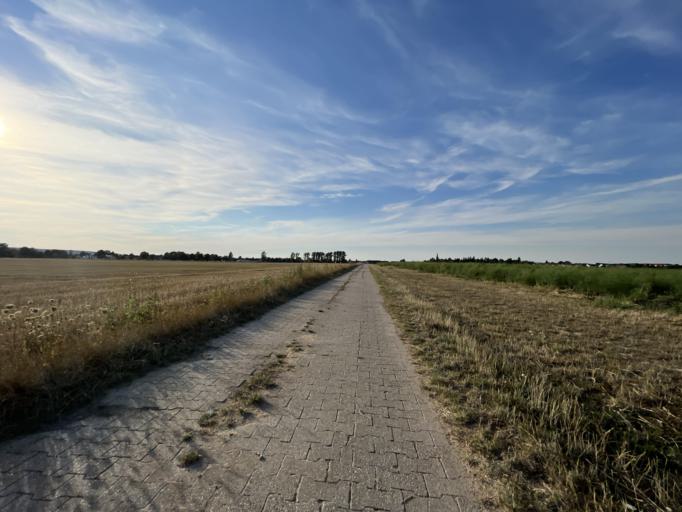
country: DE
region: North Rhine-Westphalia
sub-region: Regierungsbezirk Koln
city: Dueren
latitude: 50.7849
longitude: 6.4490
